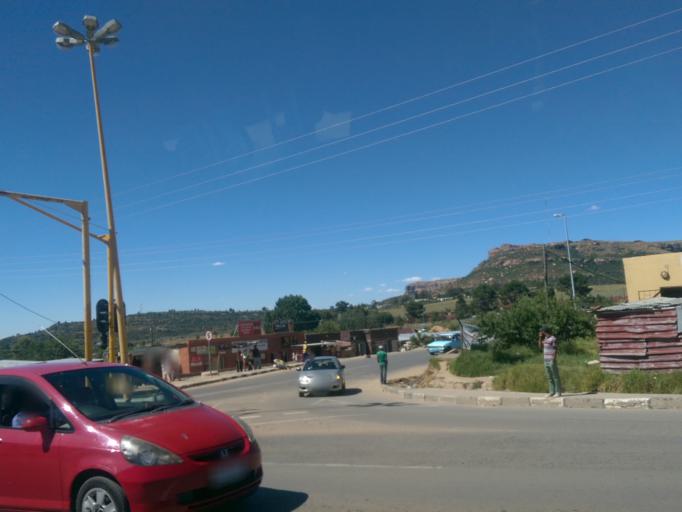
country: LS
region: Maseru
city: Maseru
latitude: -29.3470
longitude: 27.5178
